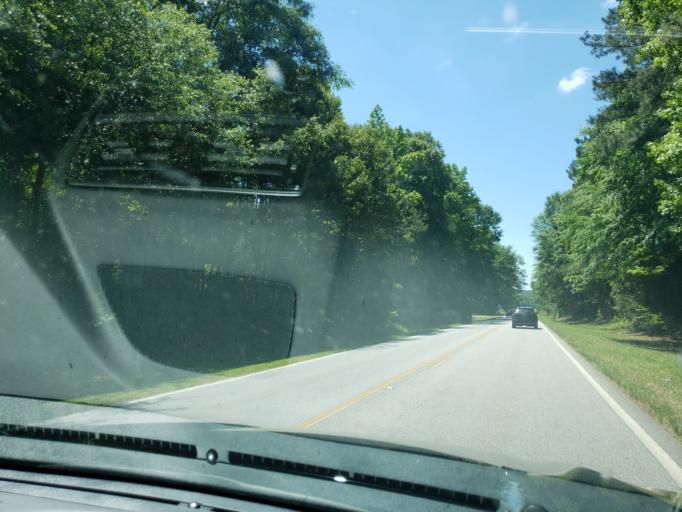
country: US
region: Alabama
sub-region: Lee County
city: Auburn
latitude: 32.6605
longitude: -85.4893
